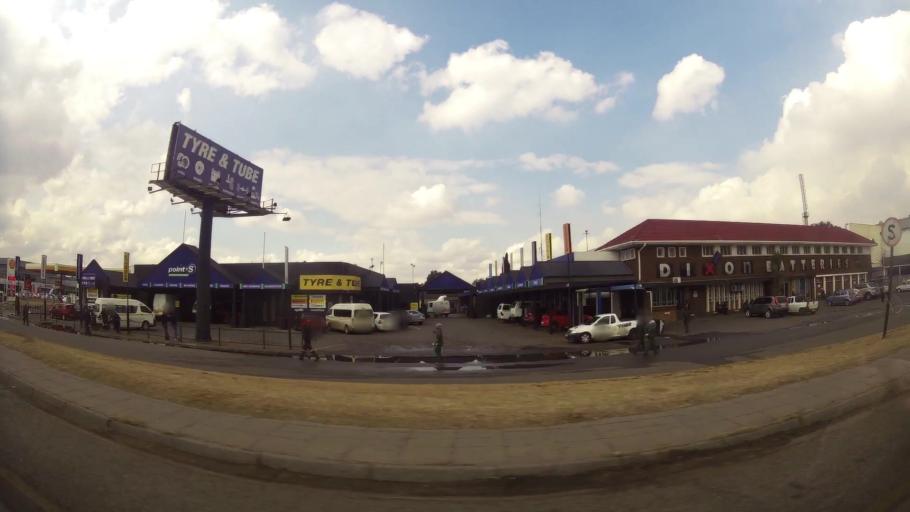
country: ZA
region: Gauteng
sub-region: Sedibeng District Municipality
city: Vereeniging
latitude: -26.6588
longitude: 27.9352
